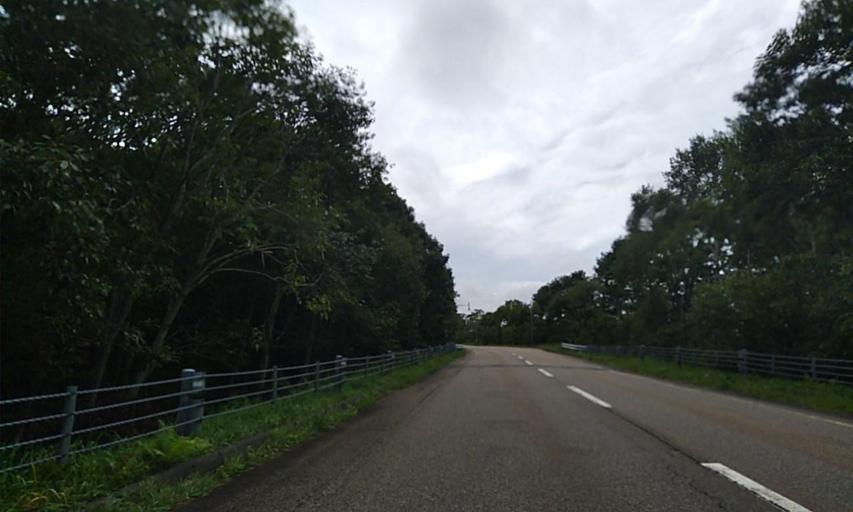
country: JP
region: Hokkaido
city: Shibetsu
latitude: 43.3534
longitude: 145.2163
